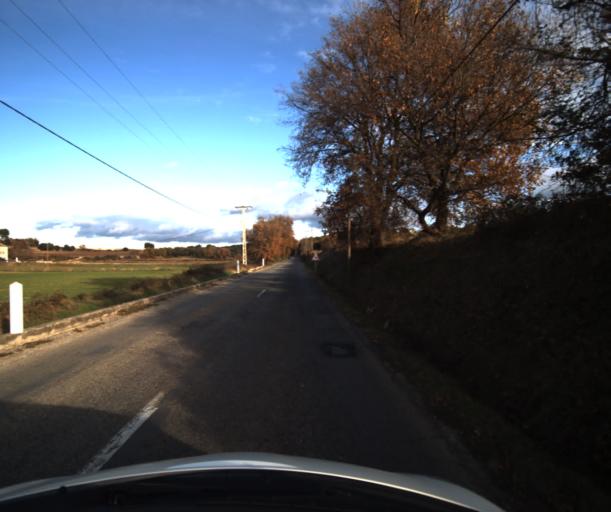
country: FR
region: Provence-Alpes-Cote d'Azur
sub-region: Departement du Vaucluse
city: Pertuis
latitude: 43.6962
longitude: 5.5376
